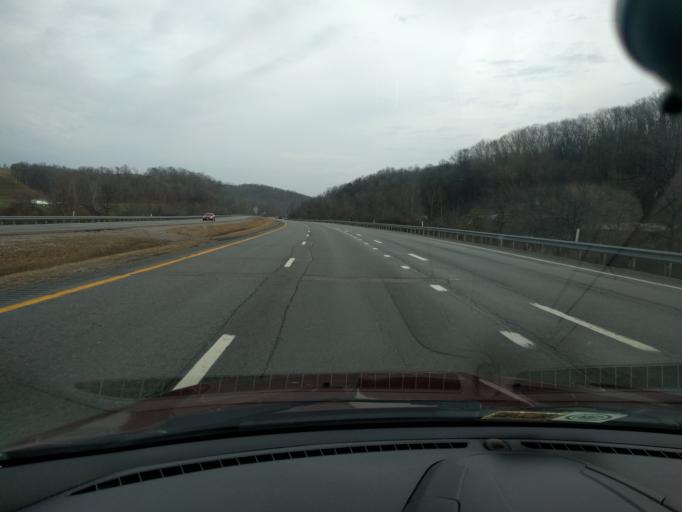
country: US
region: West Virginia
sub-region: Jackson County
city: Ravenswood
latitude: 38.9259
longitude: -81.7175
